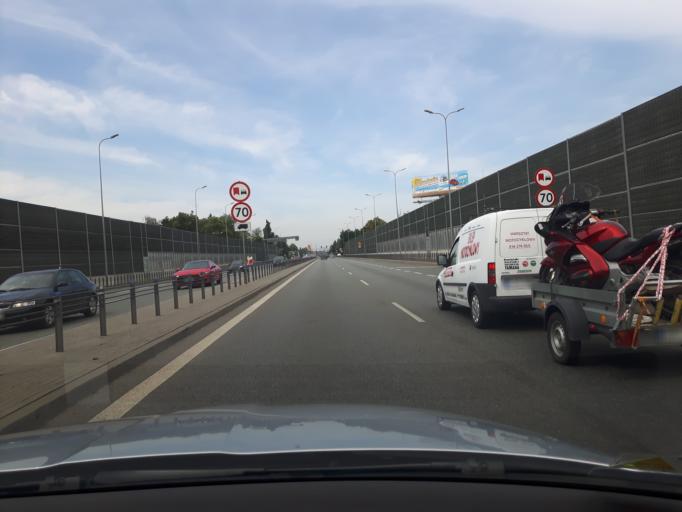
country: PL
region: Masovian Voivodeship
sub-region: Powiat warszawski zachodni
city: Lomianki
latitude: 52.3296
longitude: 20.8981
